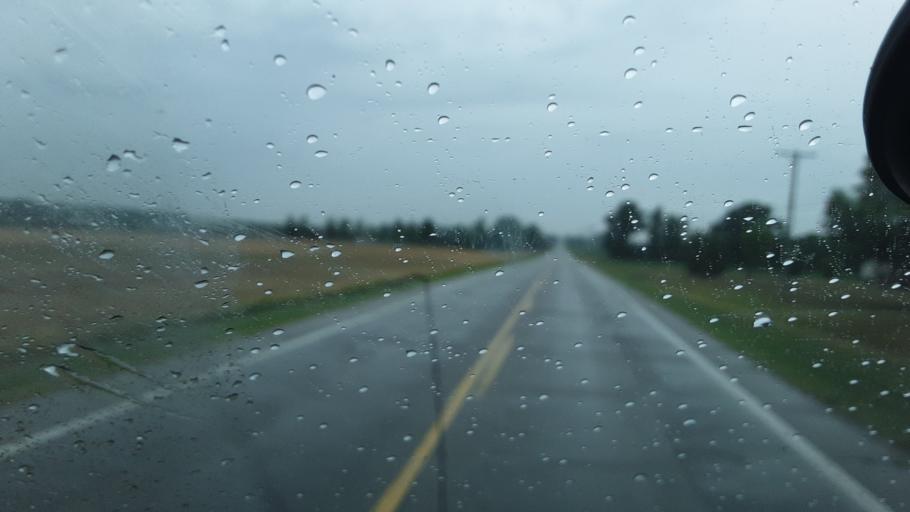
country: US
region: Ohio
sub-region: Williams County
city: Montpelier
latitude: 41.5446
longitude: -84.6130
